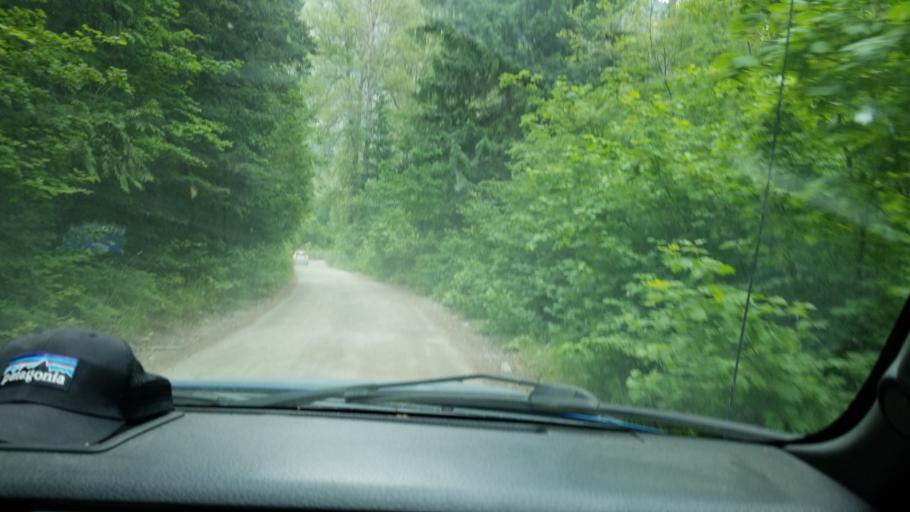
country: US
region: Washington
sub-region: Chelan County
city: Leavenworth
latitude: 47.9232
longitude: -120.9004
